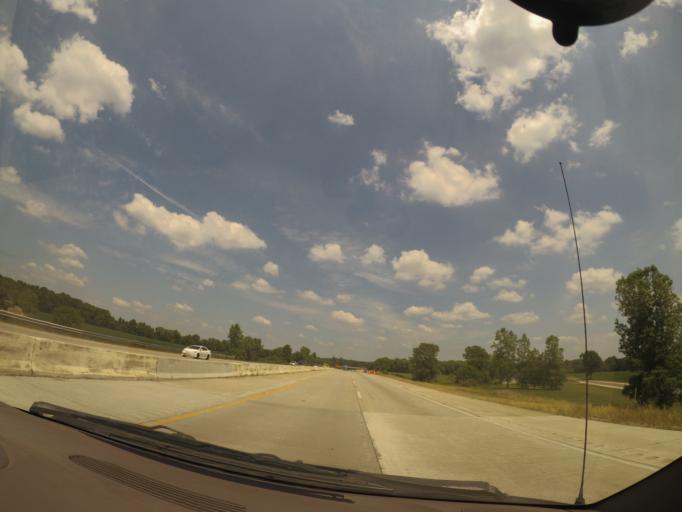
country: US
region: Indiana
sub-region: Saint Joseph County
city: Osceola
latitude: 41.6237
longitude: -86.0300
